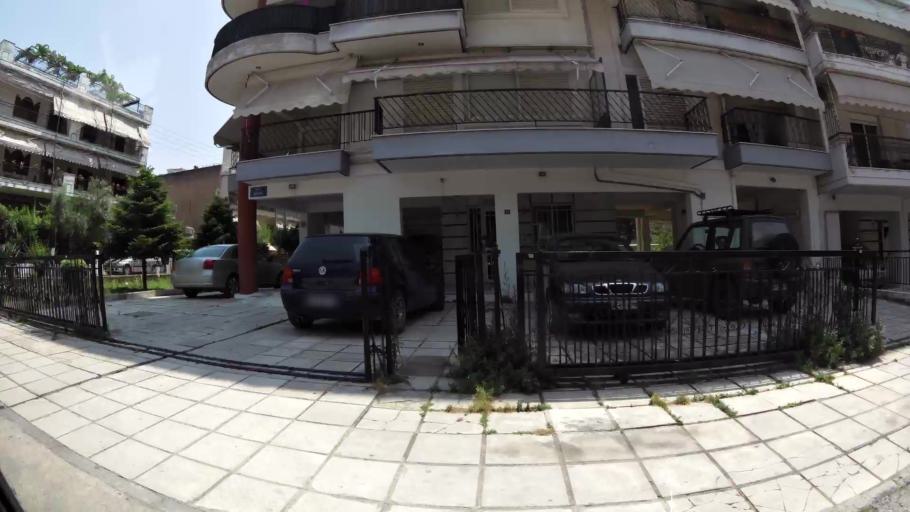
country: GR
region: Central Macedonia
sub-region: Nomos Thessalonikis
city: Menemeni
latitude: 40.6646
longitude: 22.8994
